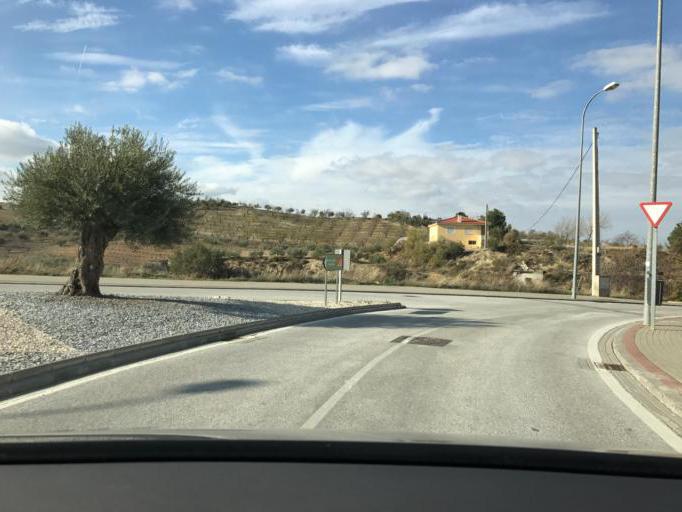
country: ES
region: Andalusia
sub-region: Provincia de Granada
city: Otura
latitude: 37.0721
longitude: -3.6370
